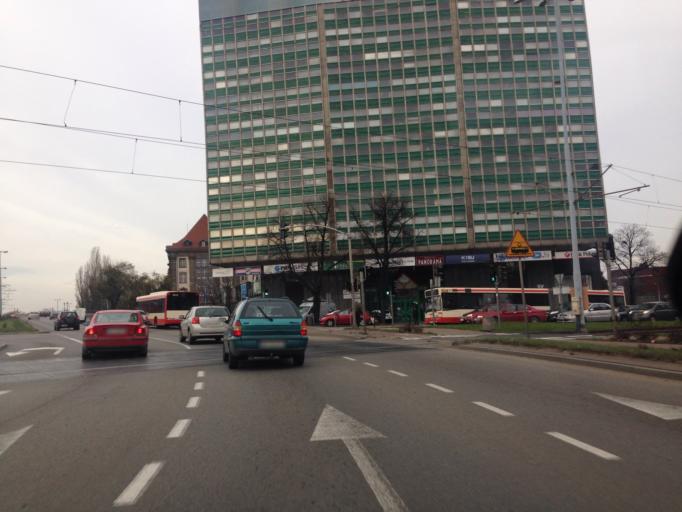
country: PL
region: Pomeranian Voivodeship
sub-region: Gdansk
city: Gdansk
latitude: 54.3577
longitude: 18.6464
